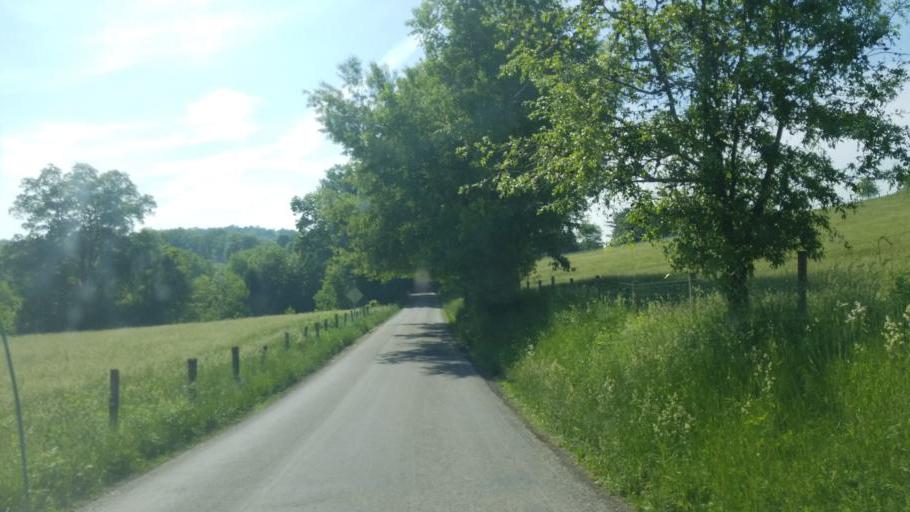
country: US
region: Ohio
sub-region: Holmes County
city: Millersburg
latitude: 40.5249
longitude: -81.8083
